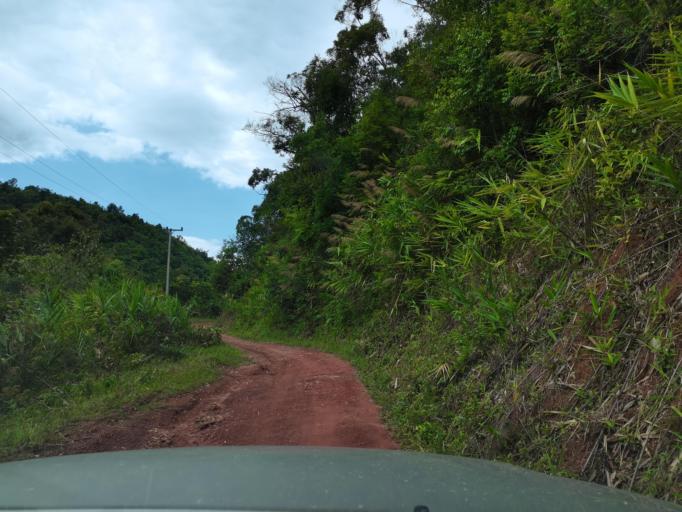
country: LA
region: Loungnamtha
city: Muang Nale
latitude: 20.5075
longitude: 101.0822
